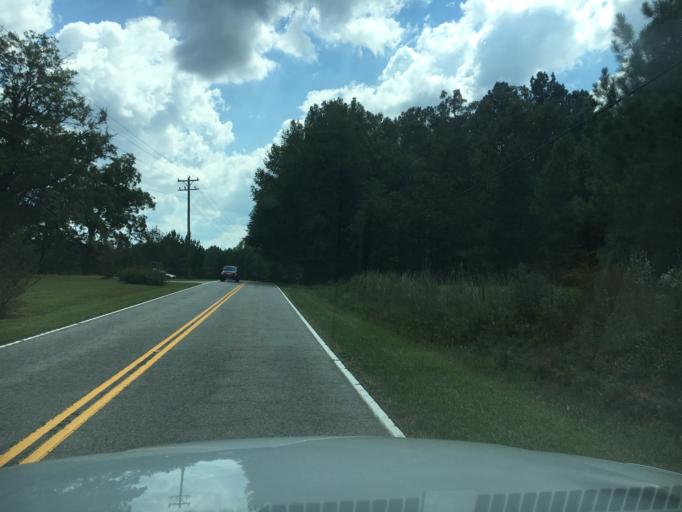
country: US
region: South Carolina
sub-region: Greenwood County
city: Greenwood
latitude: 34.1175
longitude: -82.1267
